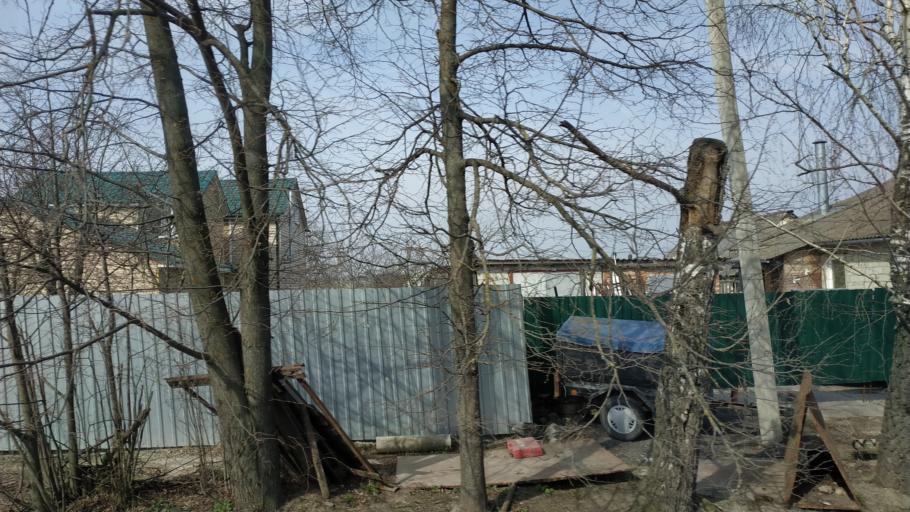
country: RU
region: Moskovskaya
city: Troitskoye
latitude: 55.3572
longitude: 38.5062
